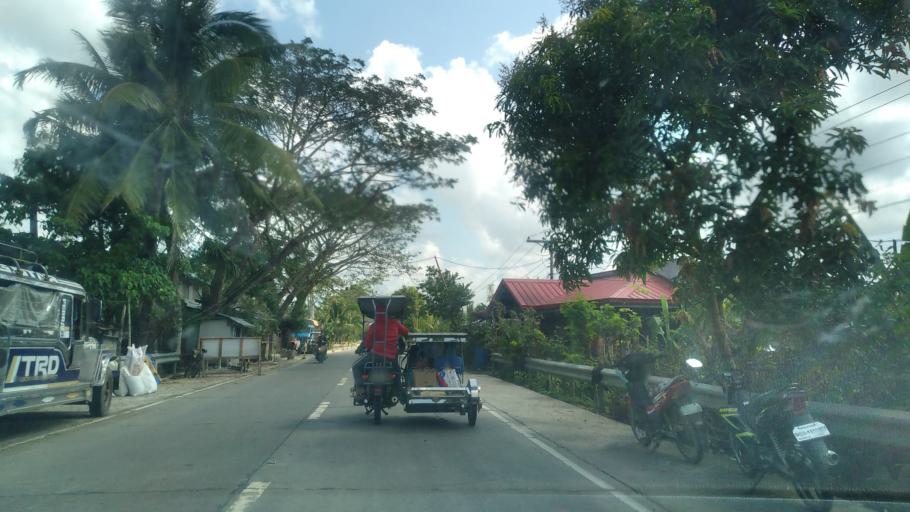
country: PH
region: Calabarzon
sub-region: Province of Quezon
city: Macalelon
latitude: 13.7564
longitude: 122.1464
